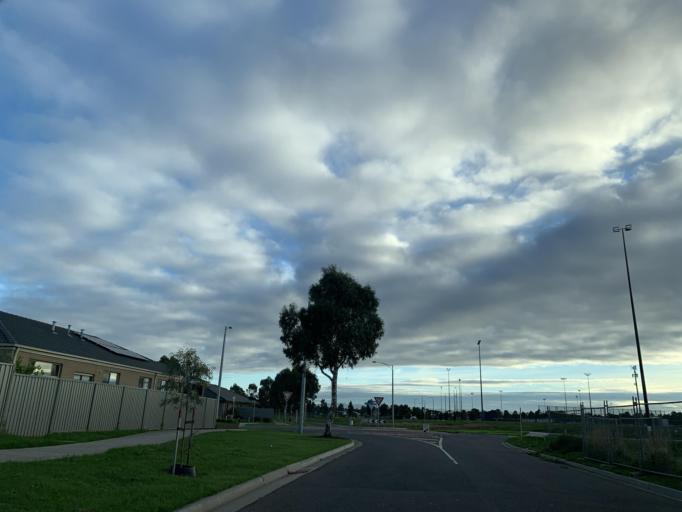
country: AU
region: Victoria
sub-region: Casey
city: Cranbourne East
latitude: -38.1256
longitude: 145.3066
